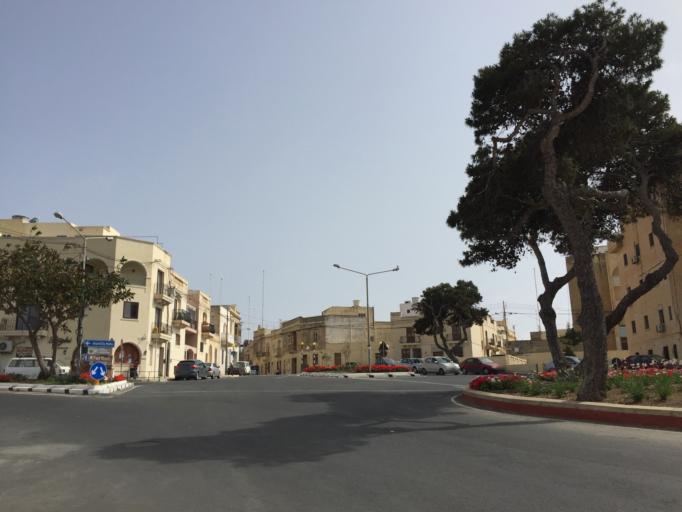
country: MT
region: Bormla
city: Cospicua
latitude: 35.8917
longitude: 14.5268
